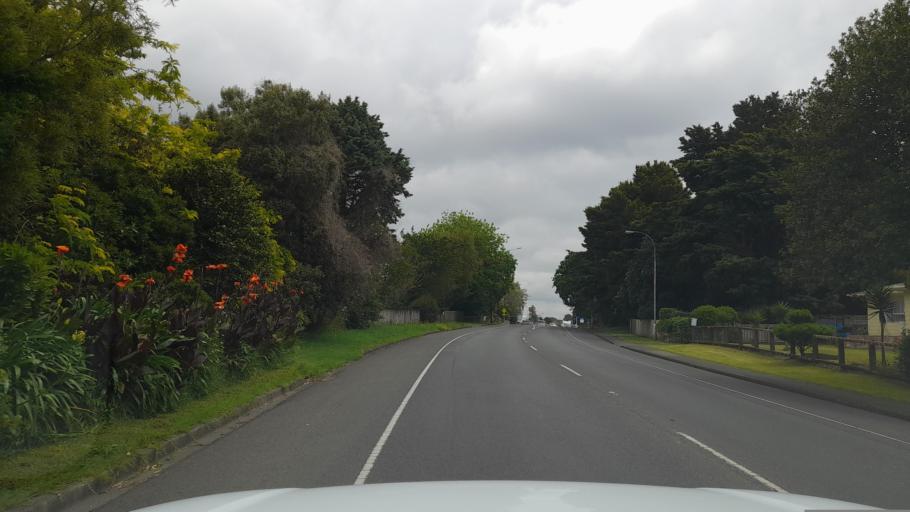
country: NZ
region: Northland
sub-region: Far North District
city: Waimate North
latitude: -35.4041
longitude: 173.8068
